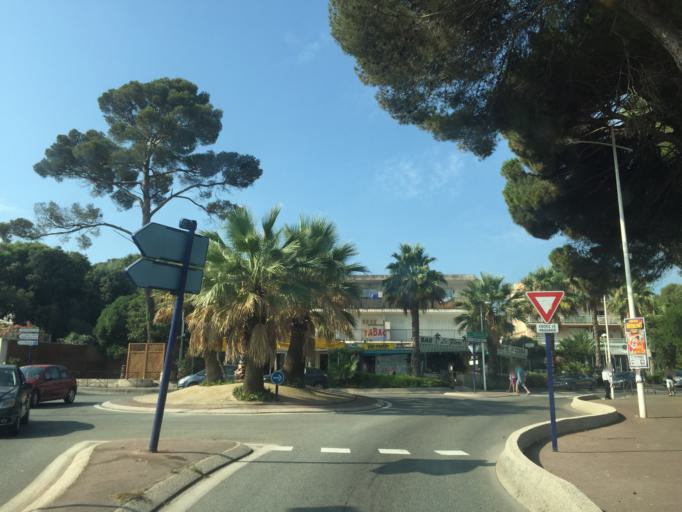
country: FR
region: Provence-Alpes-Cote d'Azur
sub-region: Departement du Var
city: Frejus
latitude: 43.3918
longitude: 6.7280
